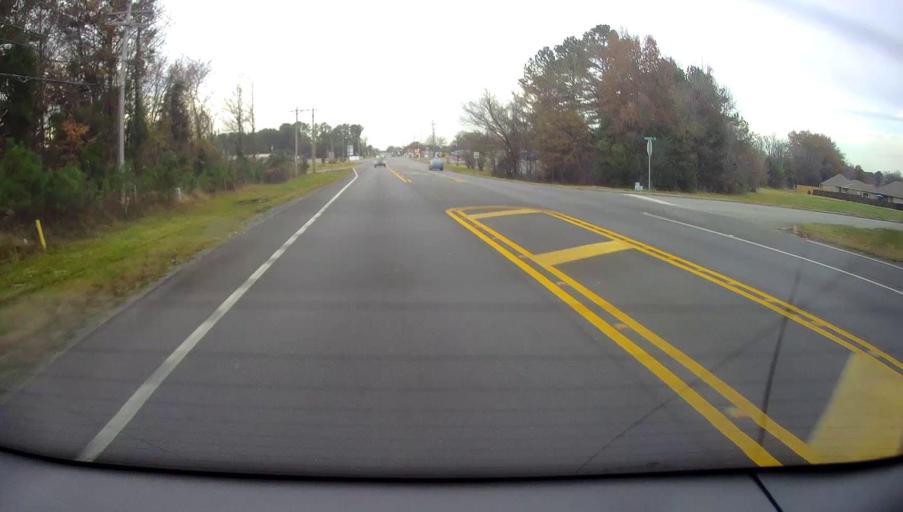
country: US
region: Alabama
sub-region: Morgan County
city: Priceville
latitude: 34.5175
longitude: -86.8846
